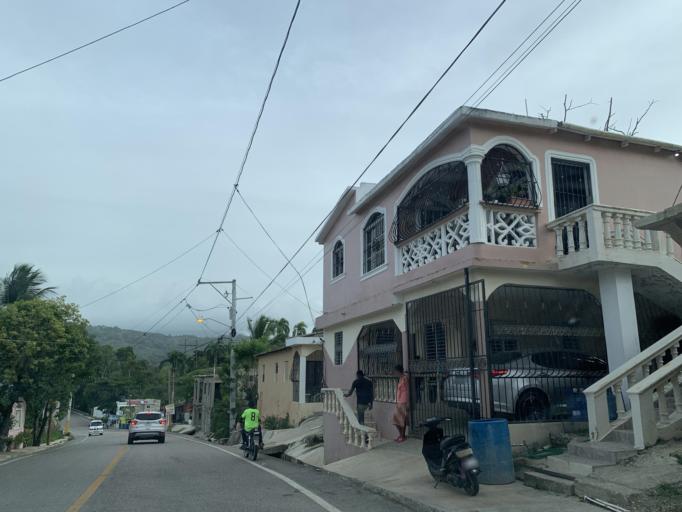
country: DO
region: Puerto Plata
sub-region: Puerto Plata
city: Puerto Plata
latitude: 19.7060
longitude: -70.6249
